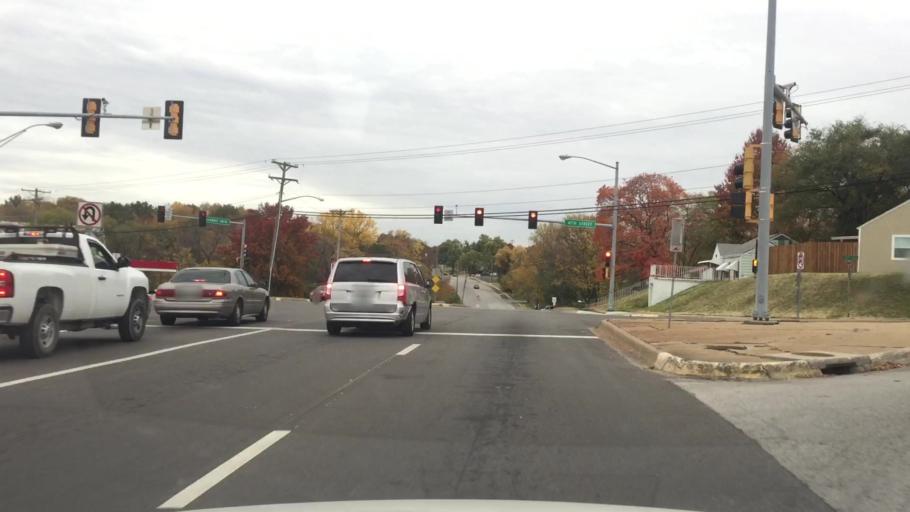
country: US
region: Kansas
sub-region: Johnson County
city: Merriam
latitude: 39.0501
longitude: -94.6861
